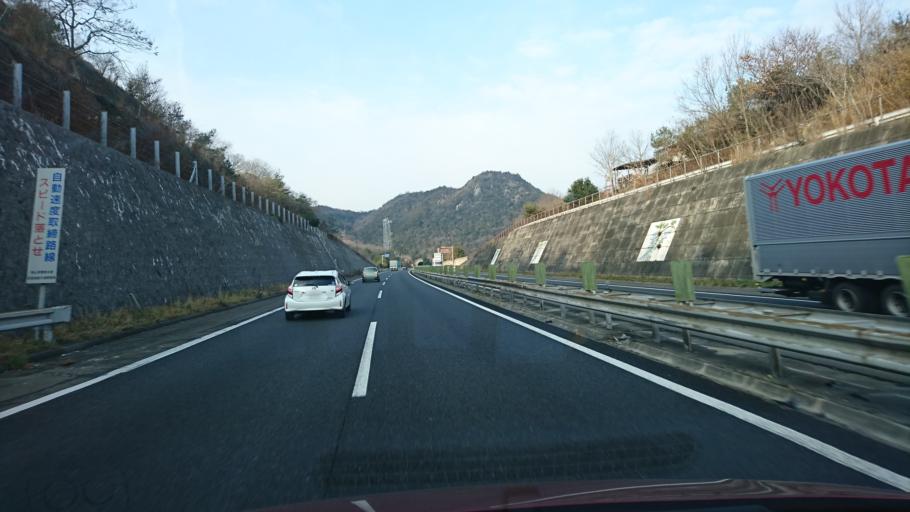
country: JP
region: Hyogo
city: Kariya
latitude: 34.7869
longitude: 134.1570
